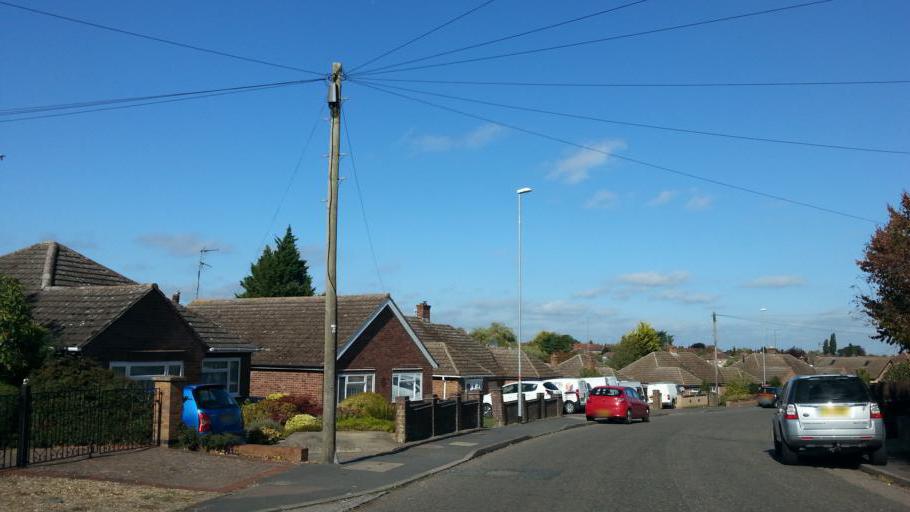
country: GB
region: England
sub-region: Northamptonshire
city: Rushden
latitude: 52.2850
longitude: -0.6038
